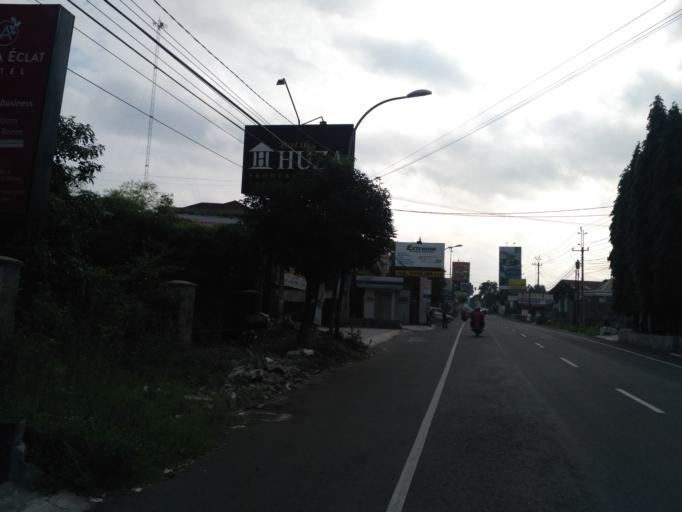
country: ID
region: Daerah Istimewa Yogyakarta
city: Melati
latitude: -7.7279
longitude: 110.3991
